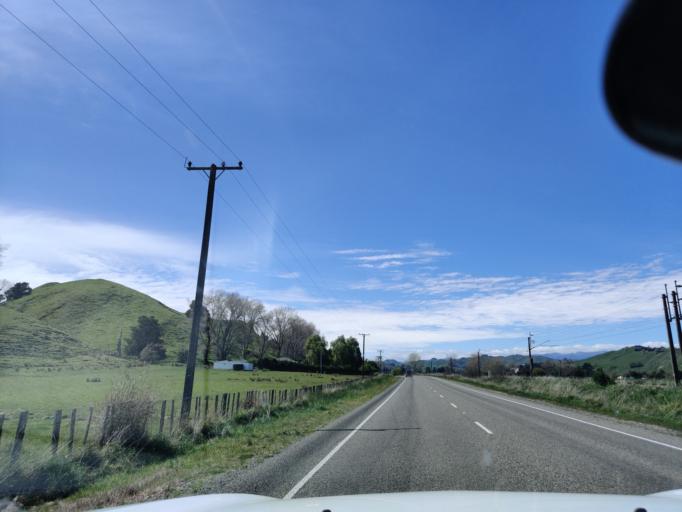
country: NZ
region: Manawatu-Wanganui
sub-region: Ruapehu District
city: Waiouru
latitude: -39.8557
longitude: 175.7240
